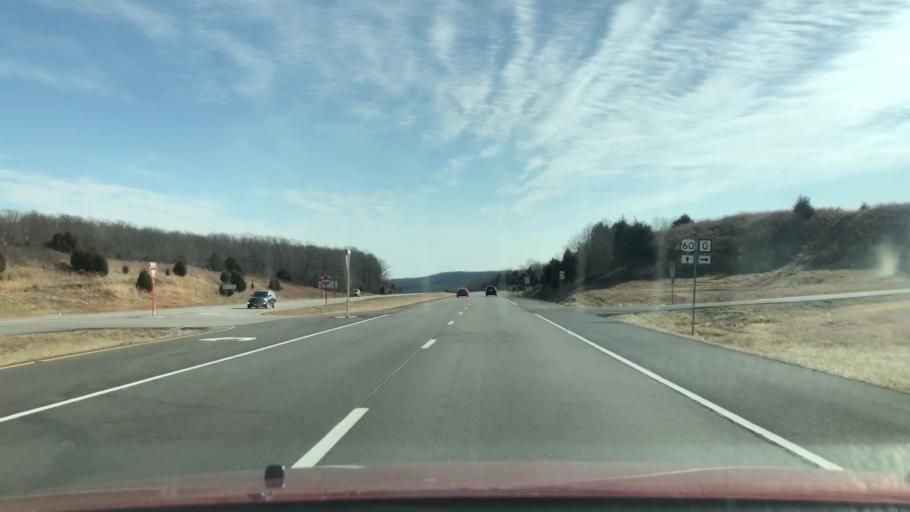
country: US
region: Missouri
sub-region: Wright County
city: Mansfield
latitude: 37.1153
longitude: -92.6753
